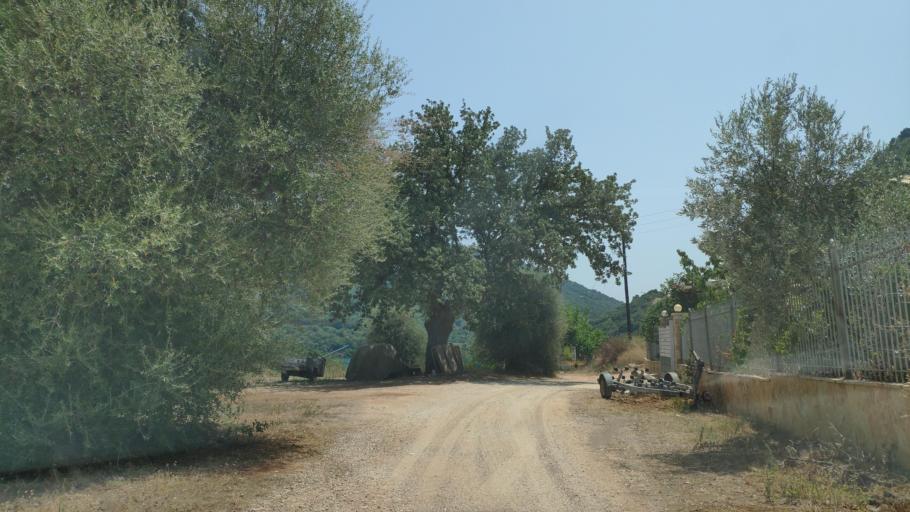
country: GR
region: West Greece
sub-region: Nomos Aitolias kai Akarnanias
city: Amfilochia
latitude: 38.8671
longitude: 21.0757
